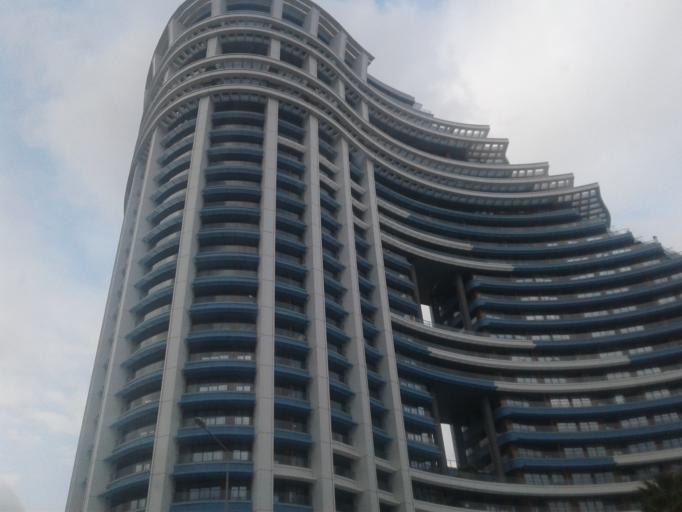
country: TR
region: Istanbul
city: Zeytinburnu
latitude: 40.9806
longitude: 28.8975
